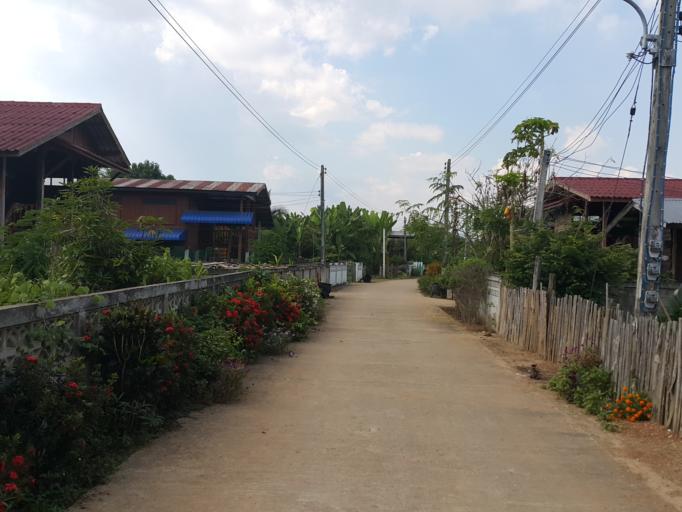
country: TH
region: Sukhothai
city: Thung Saliam
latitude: 17.3281
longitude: 99.4571
